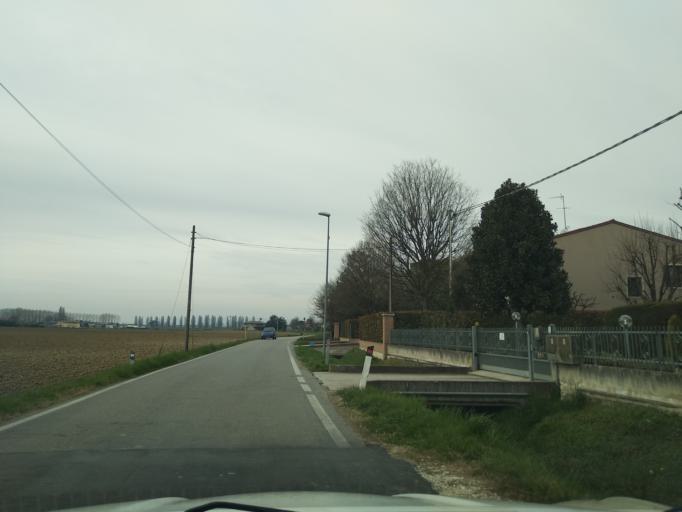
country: IT
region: Veneto
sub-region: Provincia di Padova
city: Saccolongo
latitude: 45.4086
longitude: 11.7646
